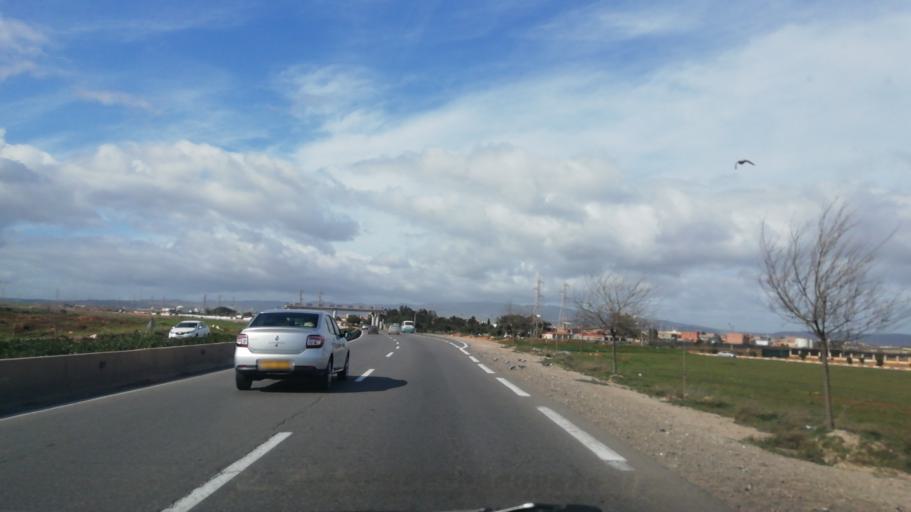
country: DZ
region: Oran
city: Ain el Bya
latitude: 35.8010
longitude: -0.2960
